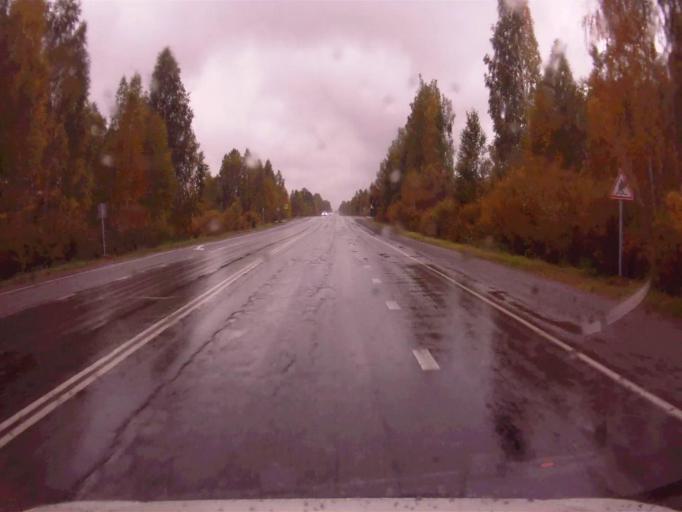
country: RU
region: Chelyabinsk
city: Argayash
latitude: 55.4868
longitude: 60.7309
